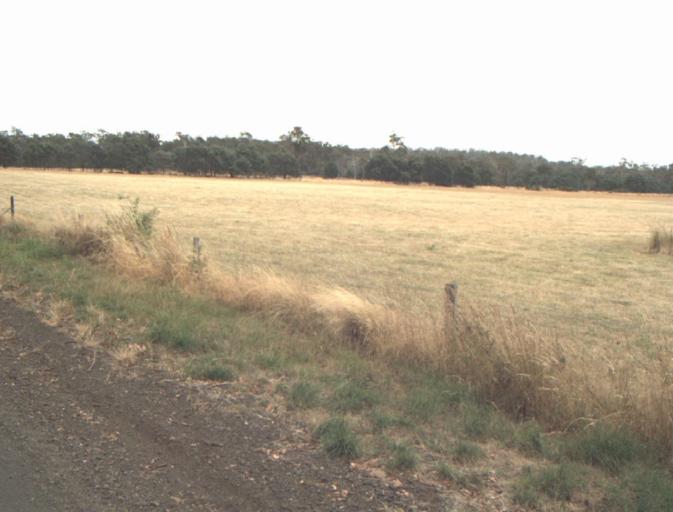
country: AU
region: Tasmania
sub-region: Northern Midlands
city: Evandale
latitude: -41.5238
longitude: 147.3655
